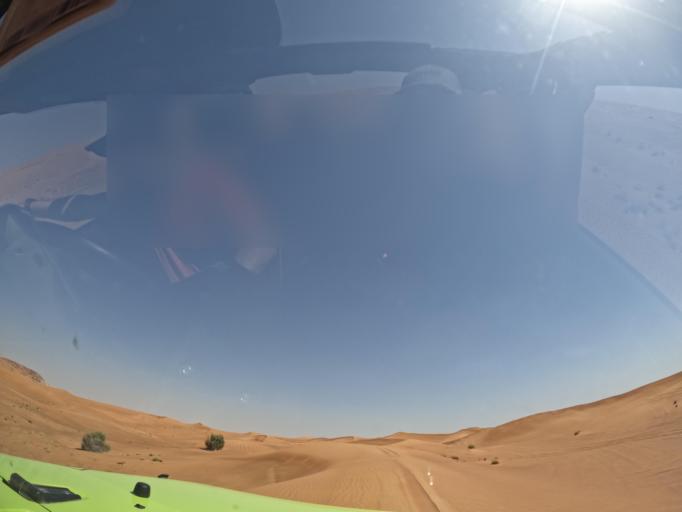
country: AE
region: Ash Shariqah
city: Adh Dhayd
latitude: 25.0058
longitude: 55.7331
